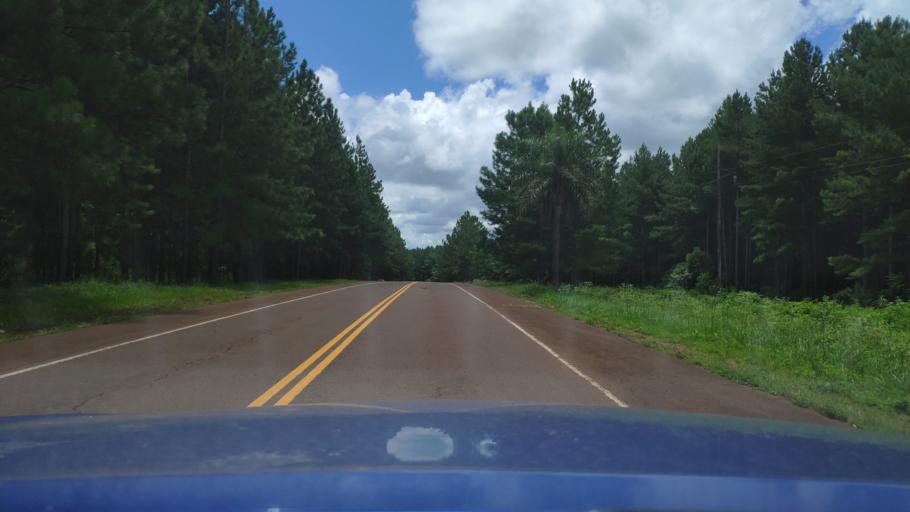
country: AR
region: Misiones
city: Dos Arroyos
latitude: -27.8056
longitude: -55.2188
